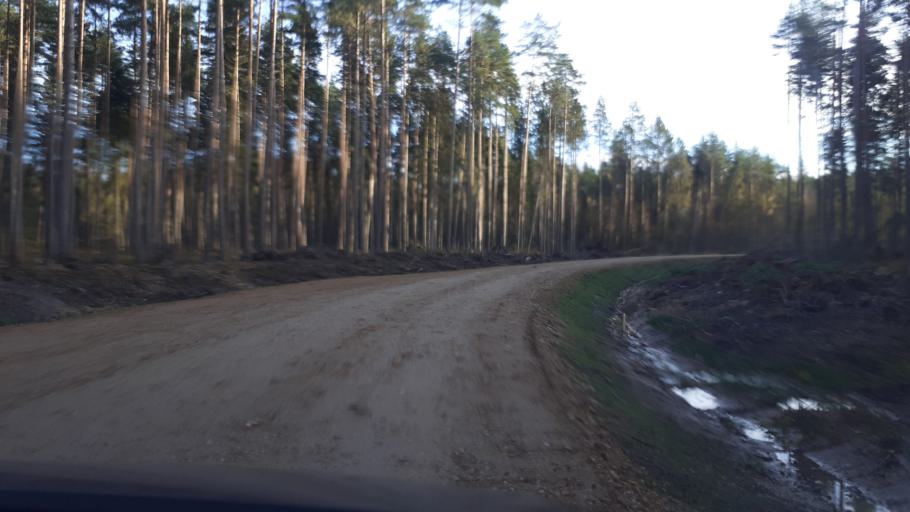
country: LV
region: Kuldigas Rajons
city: Kuldiga
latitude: 56.8501
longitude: 22.0844
